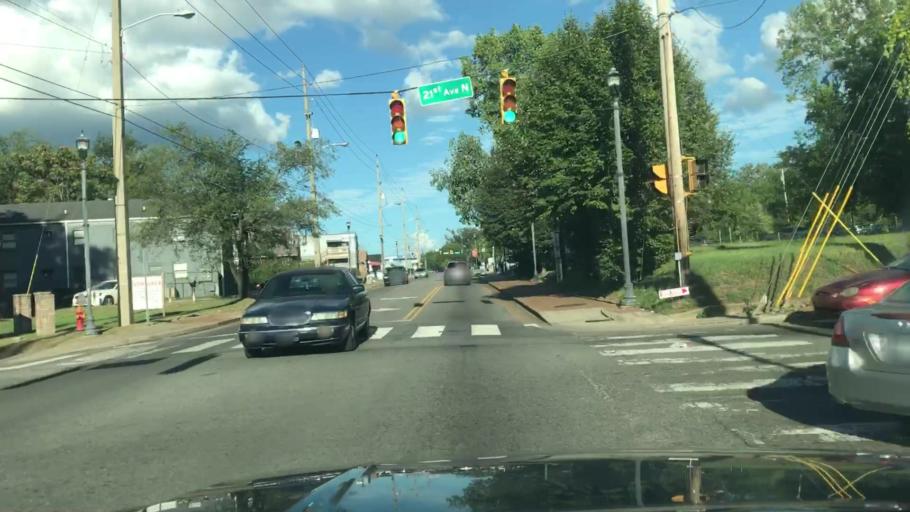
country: US
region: Tennessee
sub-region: Davidson County
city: Nashville
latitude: 36.1690
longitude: -86.8097
